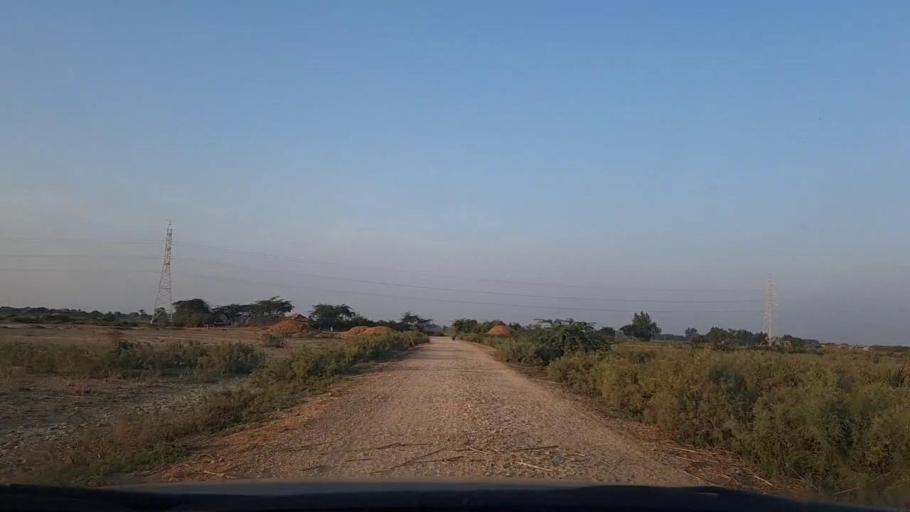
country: PK
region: Sindh
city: Mirpur Sakro
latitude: 24.5599
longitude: 67.6582
